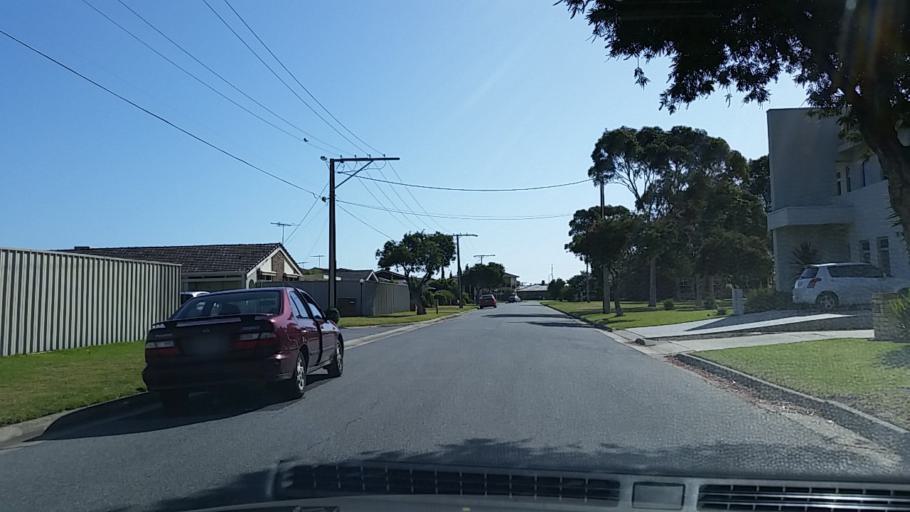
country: AU
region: South Australia
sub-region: Charles Sturt
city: Henley Beach
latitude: -34.9191
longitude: 138.5110
